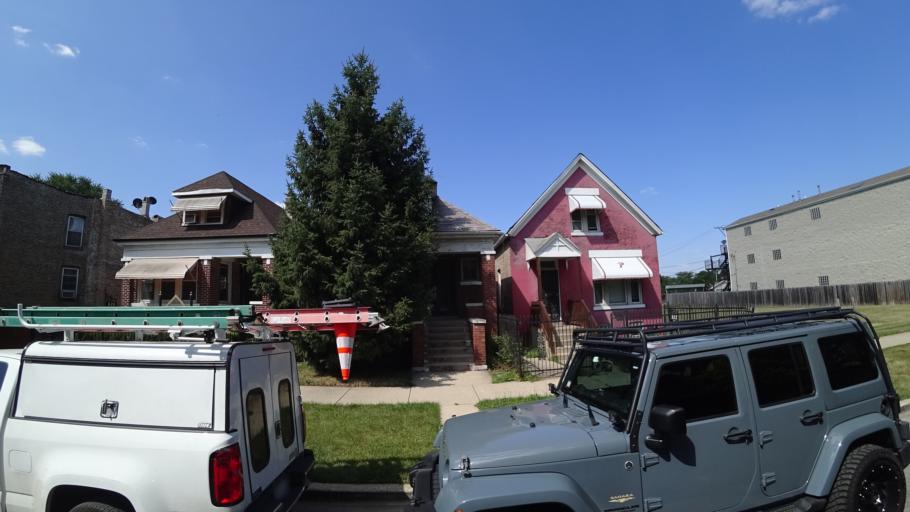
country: US
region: Illinois
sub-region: Cook County
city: Cicero
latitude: 41.8726
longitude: -87.7303
